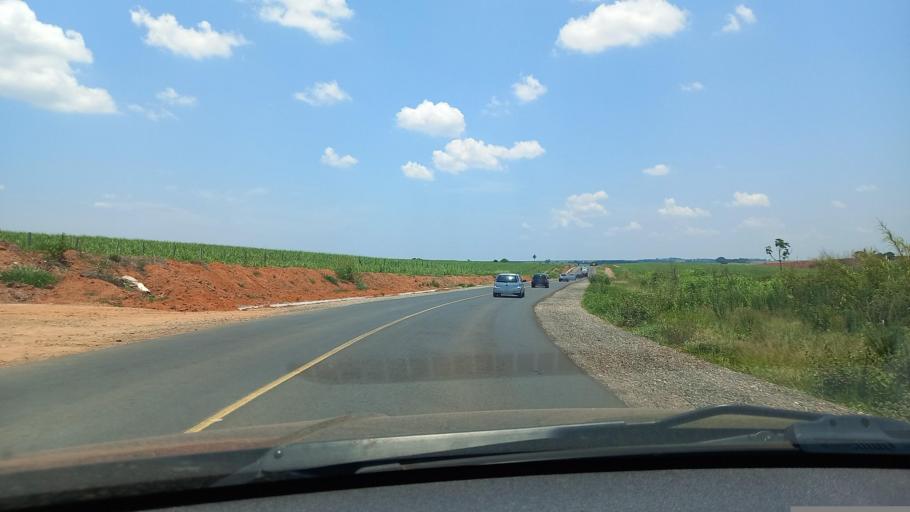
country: BR
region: Sao Paulo
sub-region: Moji-Guacu
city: Mogi-Gaucu
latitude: -22.3605
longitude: -46.8689
